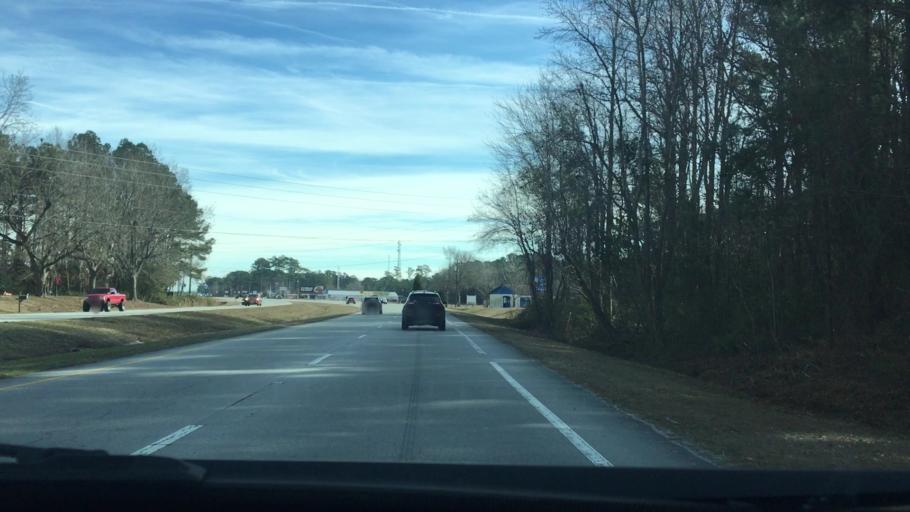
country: US
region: North Carolina
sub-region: Carteret County
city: Newport
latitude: 34.7466
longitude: -76.8342
